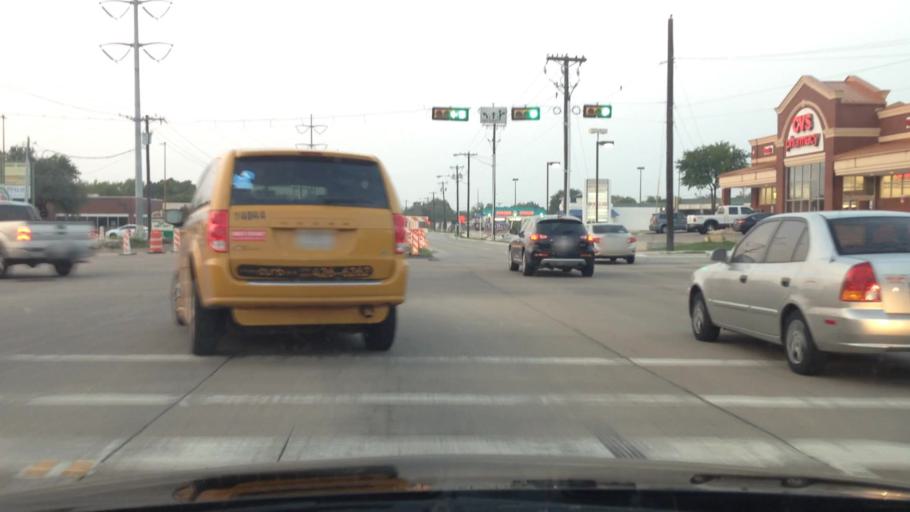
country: US
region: Texas
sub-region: Tarrant County
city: Watauga
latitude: 32.8594
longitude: -97.2378
